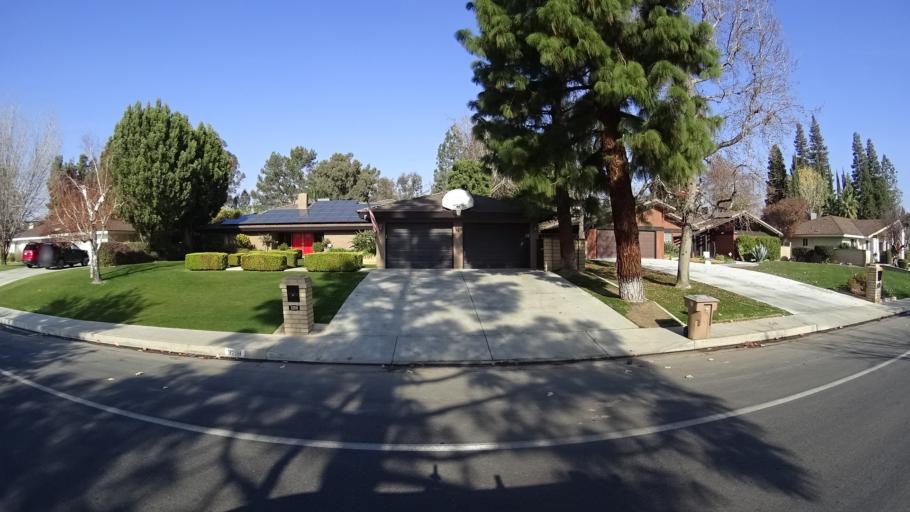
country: US
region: California
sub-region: Kern County
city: Oildale
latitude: 35.4120
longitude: -118.9565
